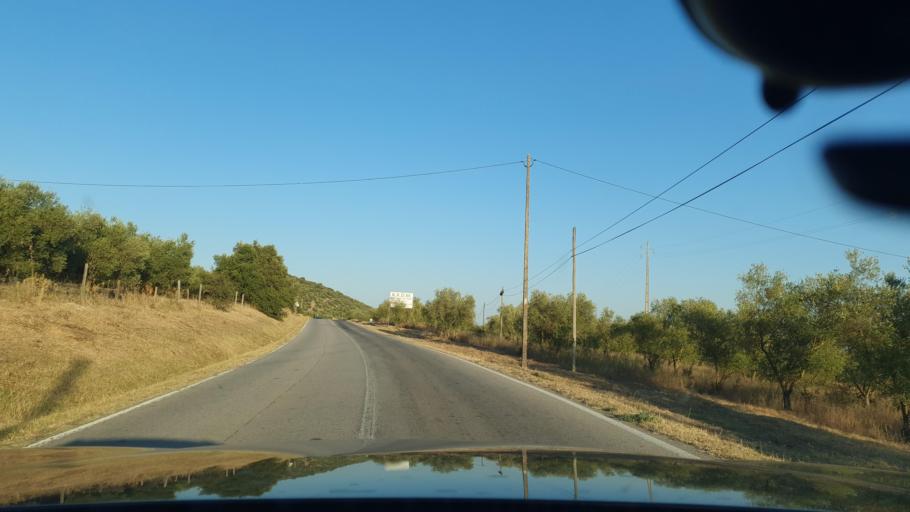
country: PT
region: Evora
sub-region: Estremoz
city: Estremoz
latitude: 38.8915
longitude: -7.6603
